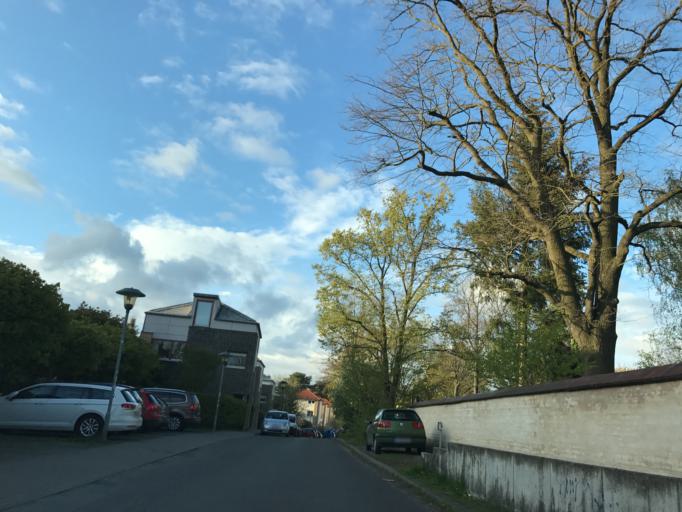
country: DE
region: Berlin
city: Kladow
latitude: 52.4689
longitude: 13.1066
